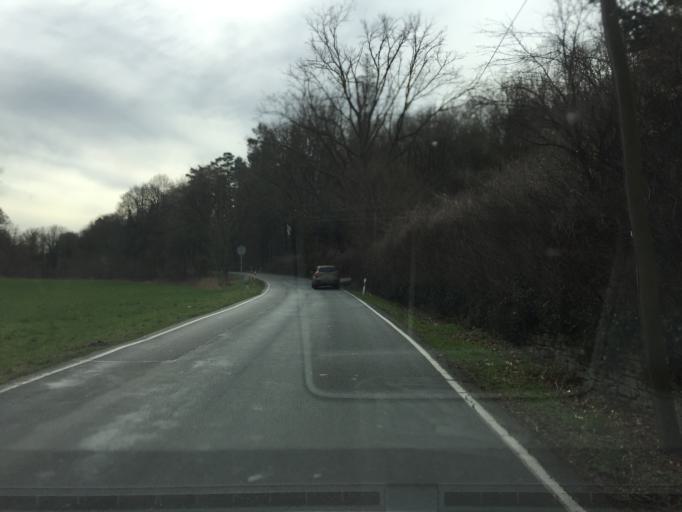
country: DE
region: North Rhine-Westphalia
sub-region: Regierungsbezirk Detmold
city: Detmold
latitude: 51.9347
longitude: 8.8326
